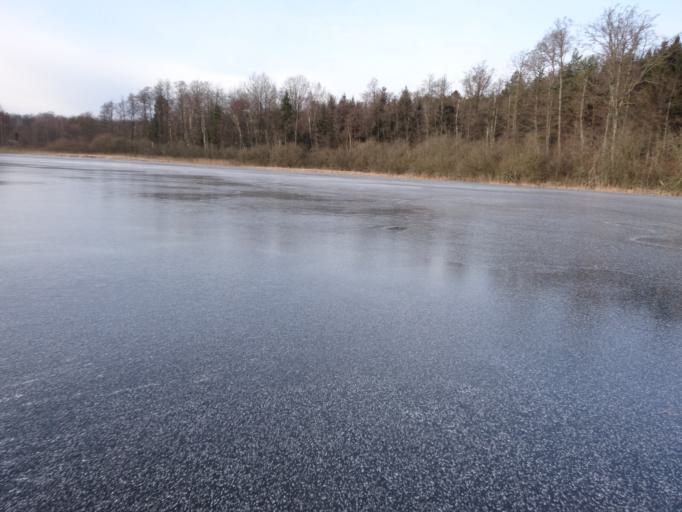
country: SE
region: Blekinge
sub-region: Karlshamns Kommun
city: Karlshamn
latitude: 56.2188
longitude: 14.9614
